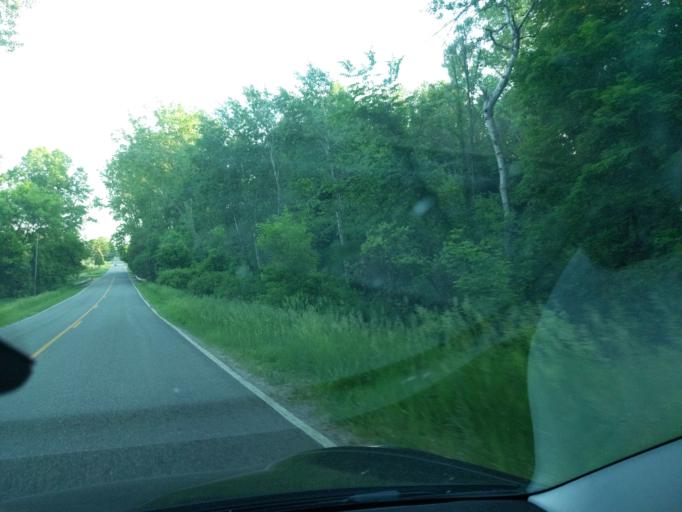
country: US
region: Michigan
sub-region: Barry County
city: Nashville
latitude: 42.5597
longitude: -85.0940
